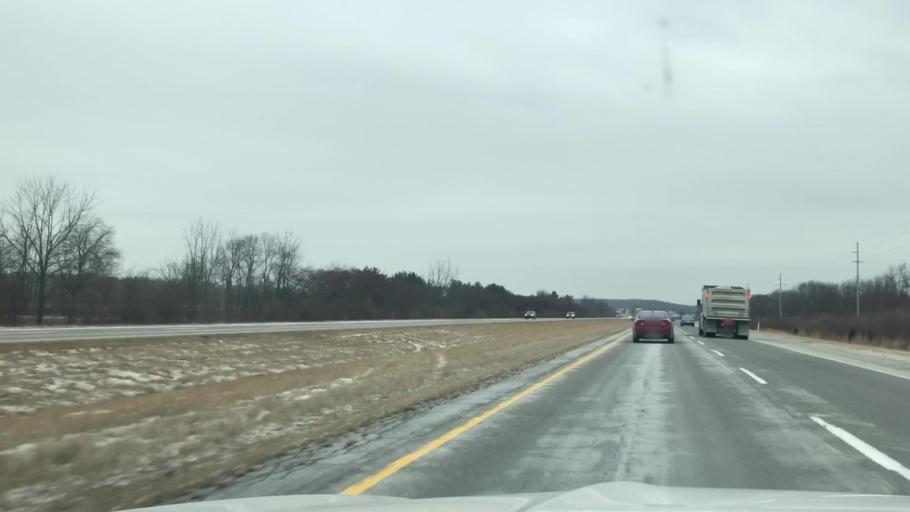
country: US
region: Indiana
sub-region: Fulton County
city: Rochester
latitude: 41.0220
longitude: -86.1765
